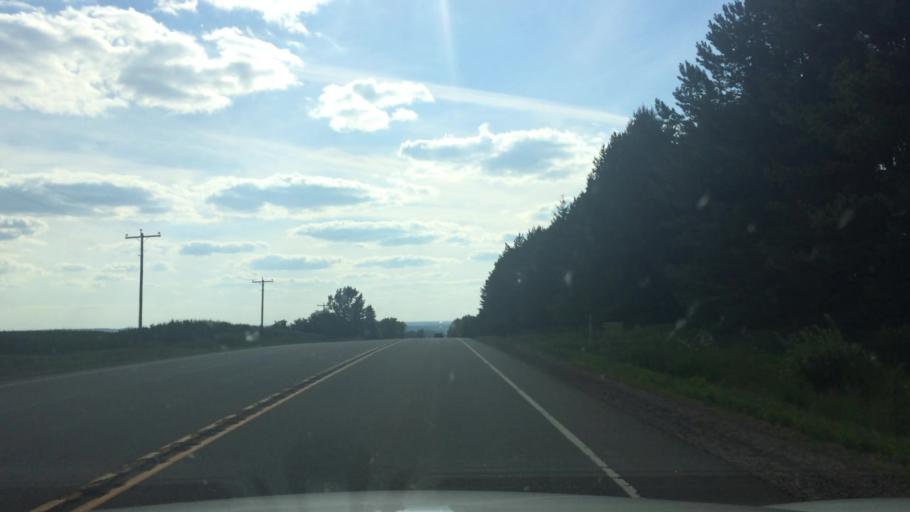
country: US
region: Wisconsin
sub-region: Lincoln County
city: Merrill
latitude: 45.1781
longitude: -89.6132
